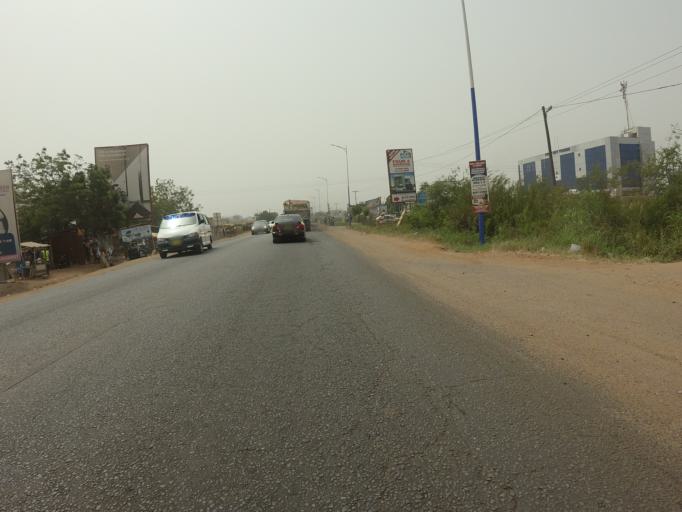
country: GH
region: Greater Accra
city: Tema
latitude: 5.7224
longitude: 0.0199
